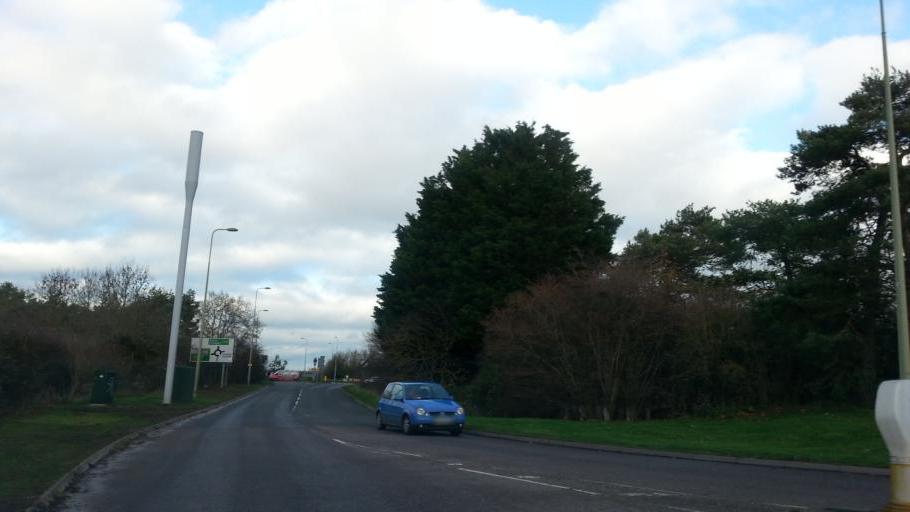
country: GB
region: England
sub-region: Oxfordshire
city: Shrivenham
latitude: 51.6142
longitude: -1.6359
